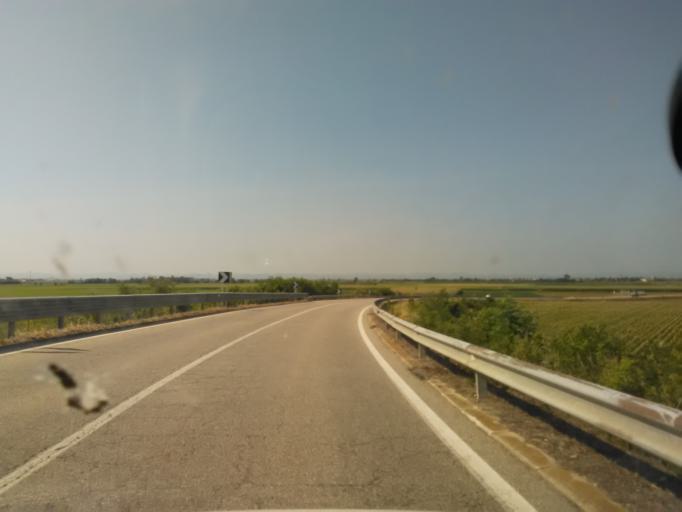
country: IT
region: Piedmont
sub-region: Provincia di Vercelli
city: Tronzano Vercellese
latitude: 45.3275
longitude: 8.1472
